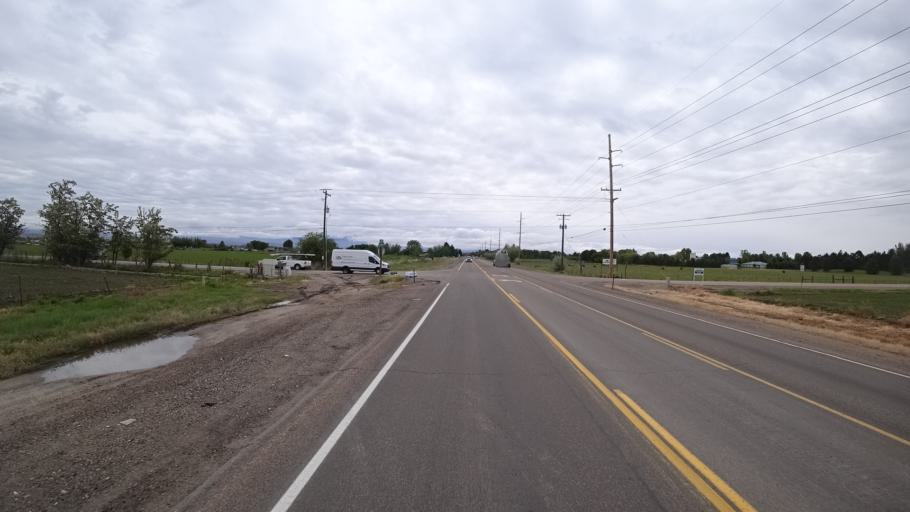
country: US
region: Idaho
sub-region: Ada County
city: Star
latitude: 43.6917
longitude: -116.4437
